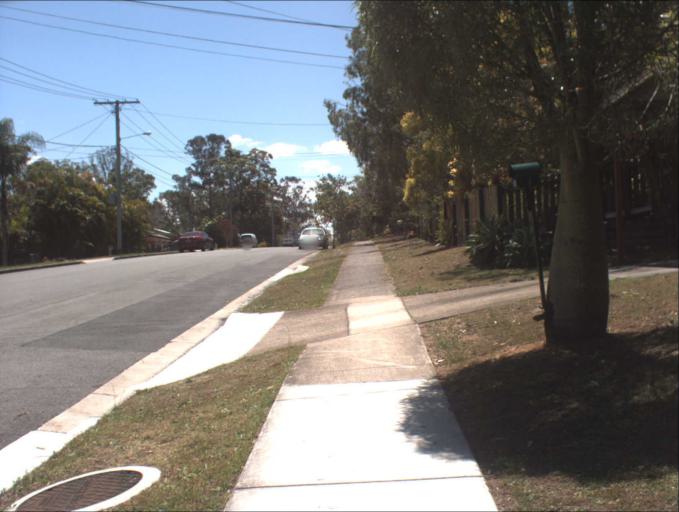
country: AU
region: Queensland
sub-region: Logan
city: Logan City
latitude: -27.6629
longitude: 153.1046
